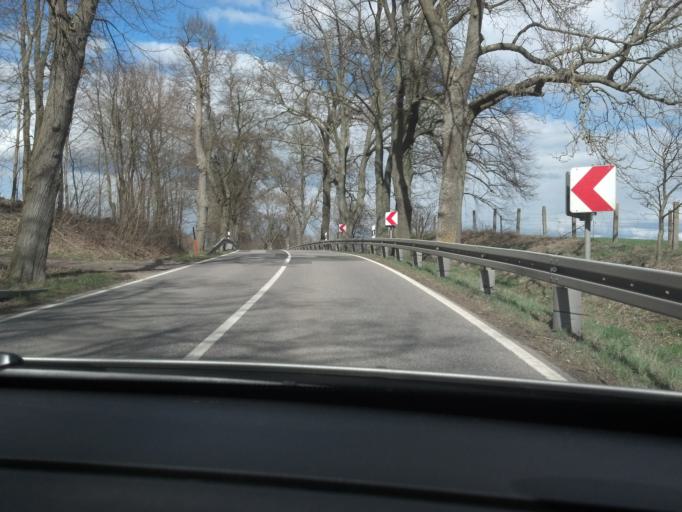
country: DE
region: Mecklenburg-Vorpommern
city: Loitz
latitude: 53.4066
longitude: 13.3644
